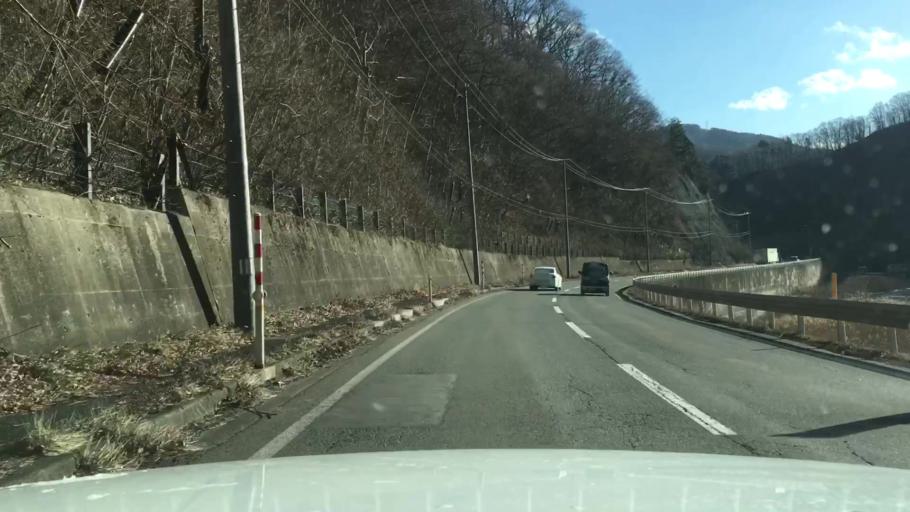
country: JP
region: Iwate
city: Tono
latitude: 39.6493
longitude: 141.5836
